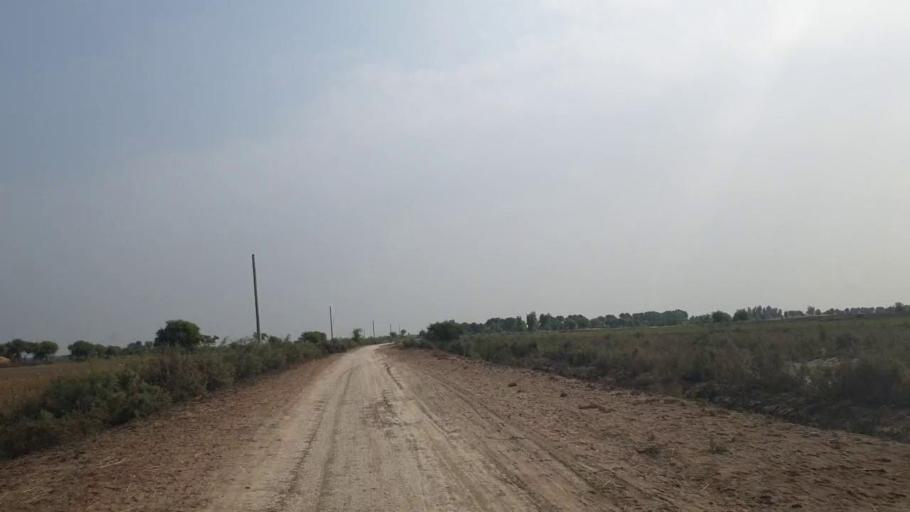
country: PK
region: Sindh
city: Badin
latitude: 24.7632
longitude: 68.7866
